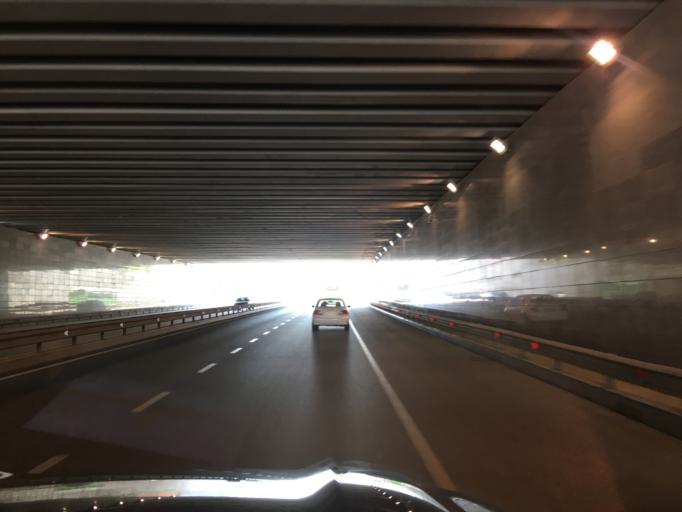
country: TM
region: Ahal
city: Ashgabat
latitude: 37.9423
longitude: 58.3659
